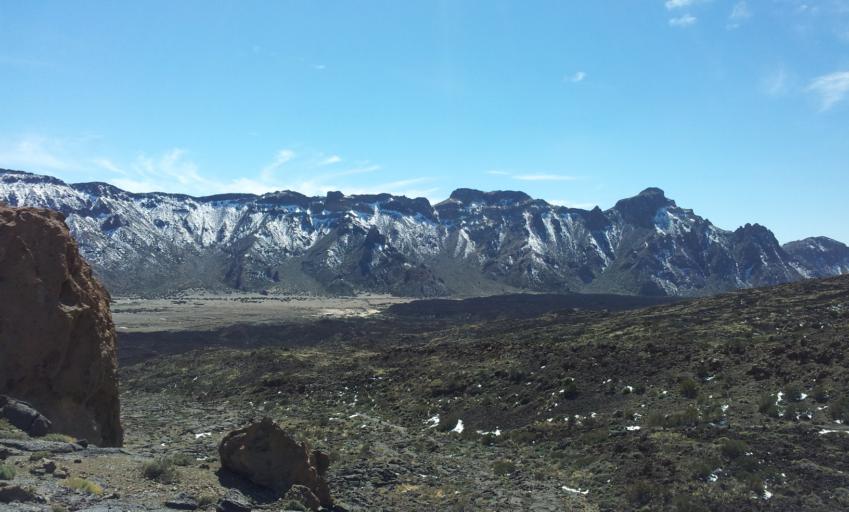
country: ES
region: Canary Islands
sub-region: Provincia de Santa Cruz de Tenerife
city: Vilaflor
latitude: 28.2305
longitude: -16.6399
